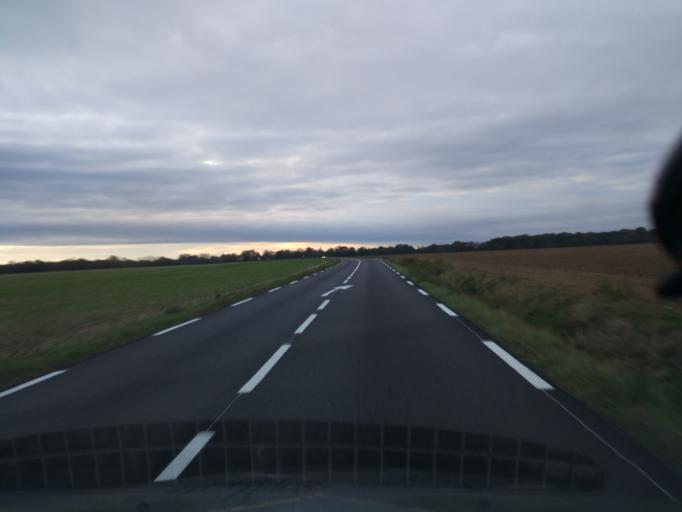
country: FR
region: Ile-de-France
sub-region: Departement de l'Essonne
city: Les Molieres
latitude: 48.6590
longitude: 2.0666
